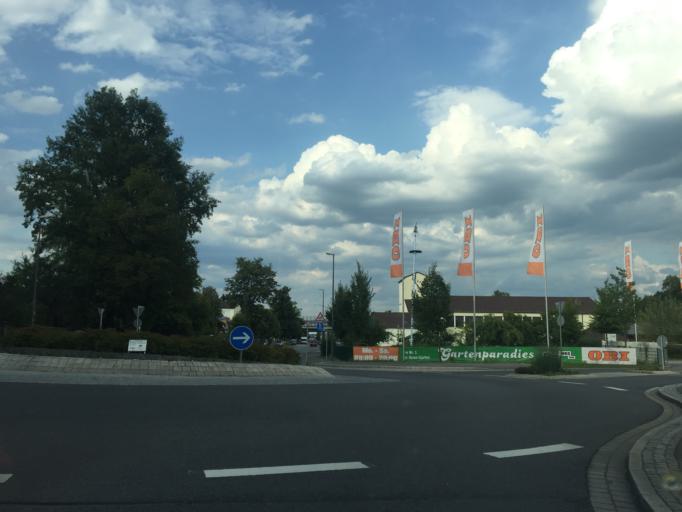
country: DE
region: Bavaria
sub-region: Upper Palatinate
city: Schirmitz
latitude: 49.6551
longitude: 12.1429
